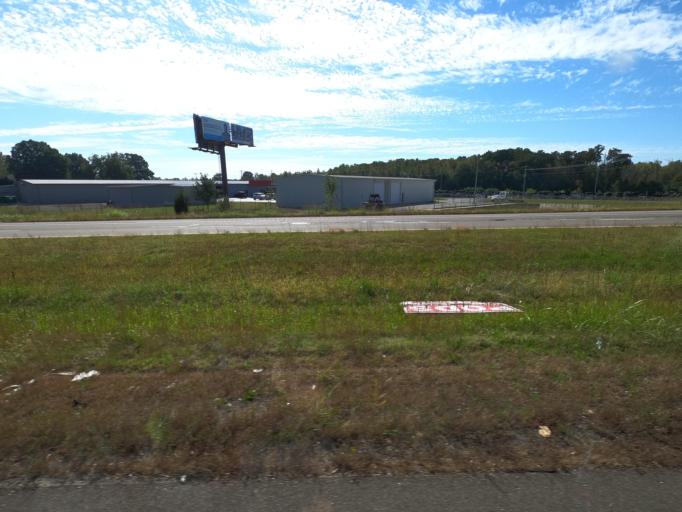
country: US
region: Tennessee
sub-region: Madison County
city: Jackson
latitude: 35.6670
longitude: -88.8877
